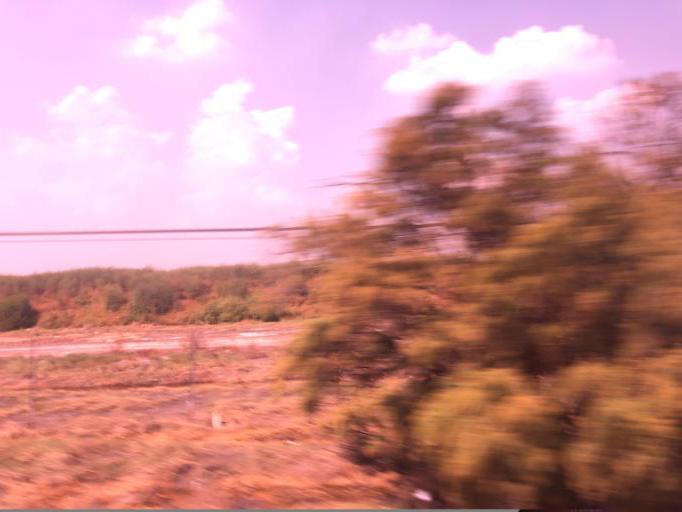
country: MX
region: Mexico
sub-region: Ciudad Nezahualcoyotl
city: Colonia Gustavo Baz Prada
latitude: 19.4640
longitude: -99.0197
